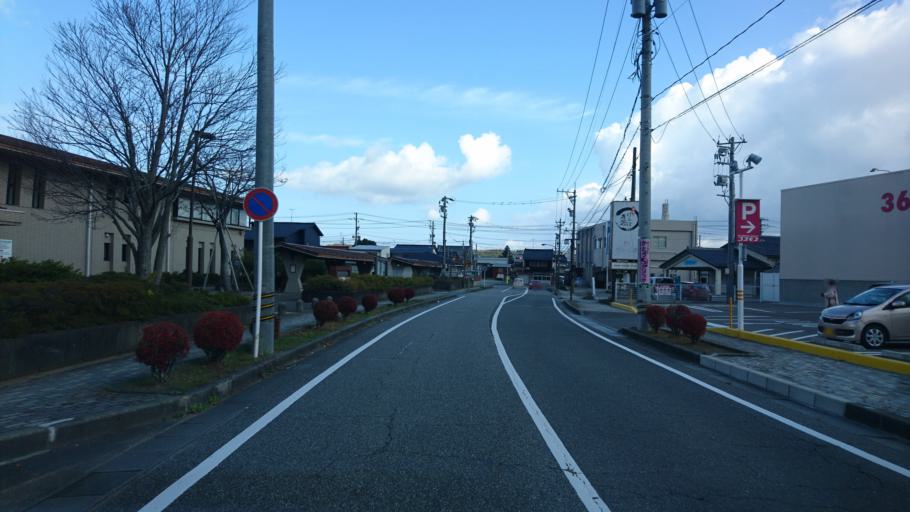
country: JP
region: Fukui
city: Maruoka
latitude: 36.3022
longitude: 136.3112
